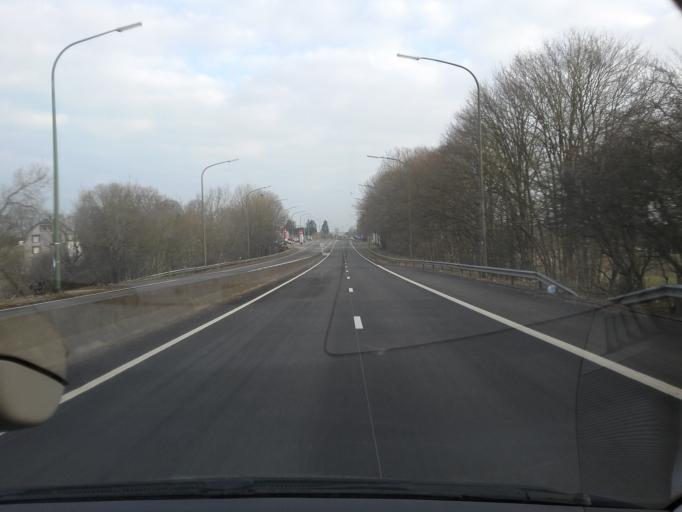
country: BE
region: Wallonia
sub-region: Province du Luxembourg
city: Fauvillers
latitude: 49.8950
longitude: 5.7004
